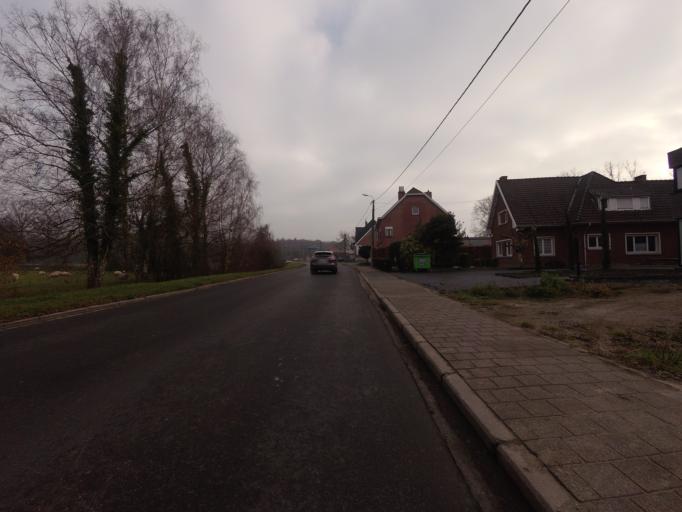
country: BE
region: Flanders
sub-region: Provincie Vlaams-Brabant
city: Galmaarden
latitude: 50.8047
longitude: 3.9629
